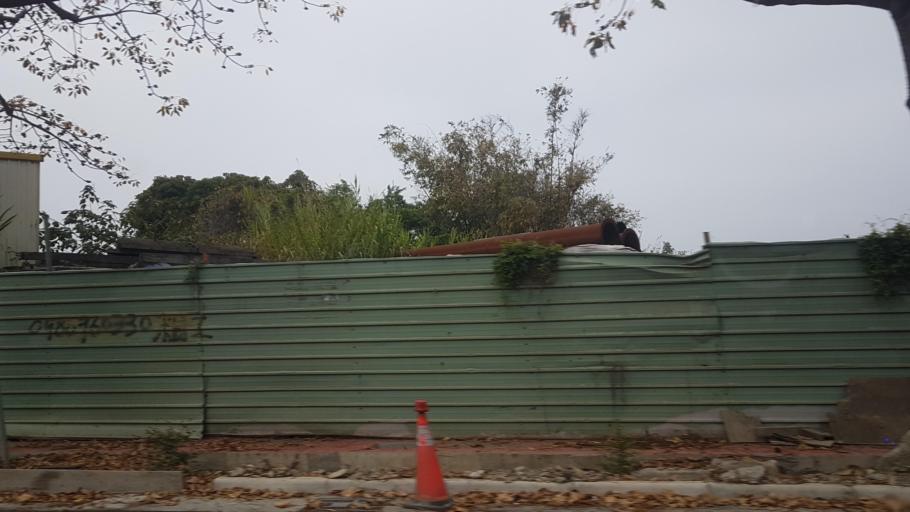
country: TW
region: Taiwan
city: Xinying
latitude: 23.3160
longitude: 120.3028
